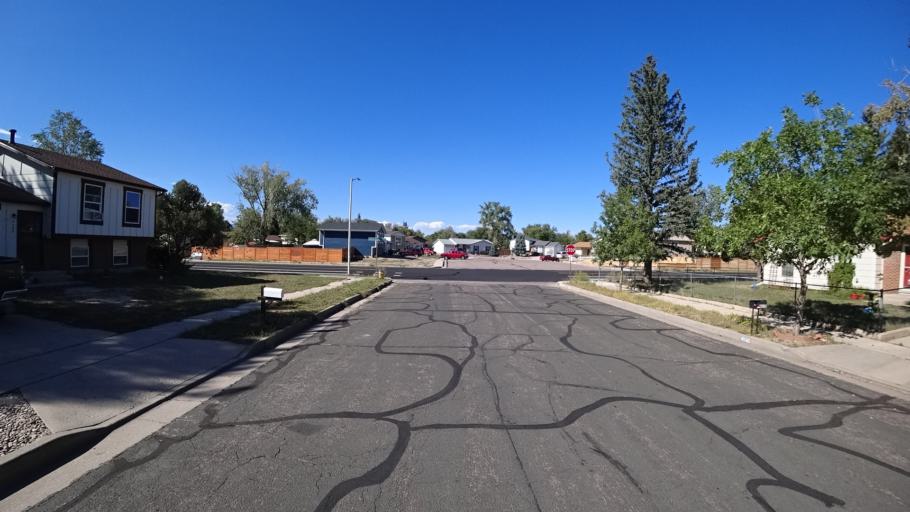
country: US
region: Colorado
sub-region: El Paso County
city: Stratmoor
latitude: 38.7966
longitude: -104.7503
